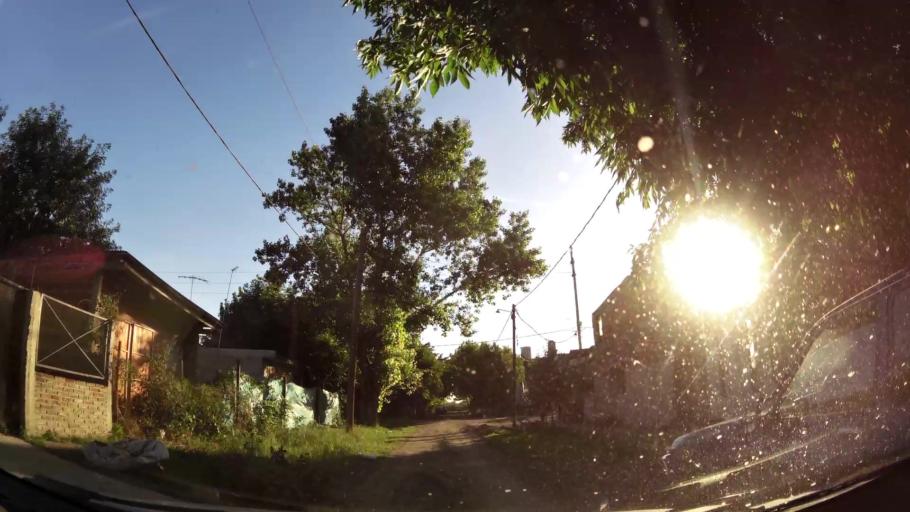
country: AR
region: Buenos Aires
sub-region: Partido de Merlo
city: Merlo
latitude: -34.6990
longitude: -58.7567
